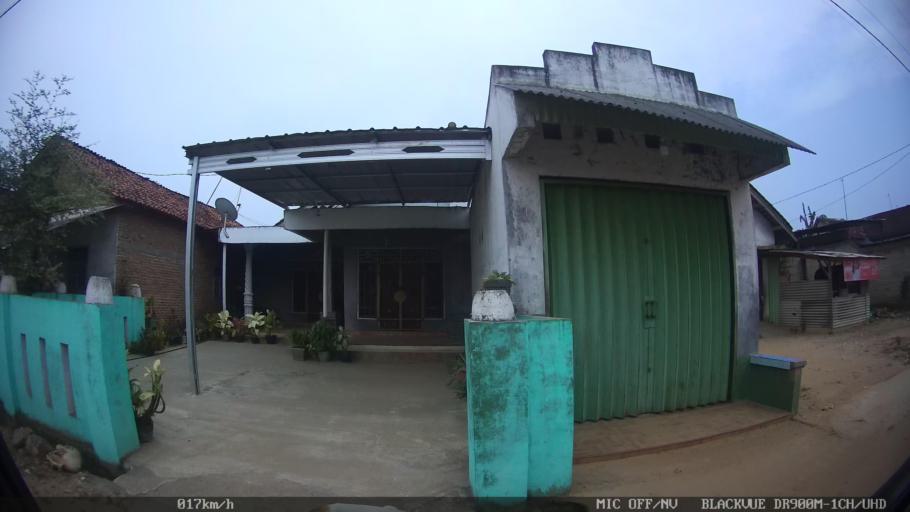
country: ID
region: Lampung
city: Panjang
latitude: -5.4180
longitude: 105.3564
